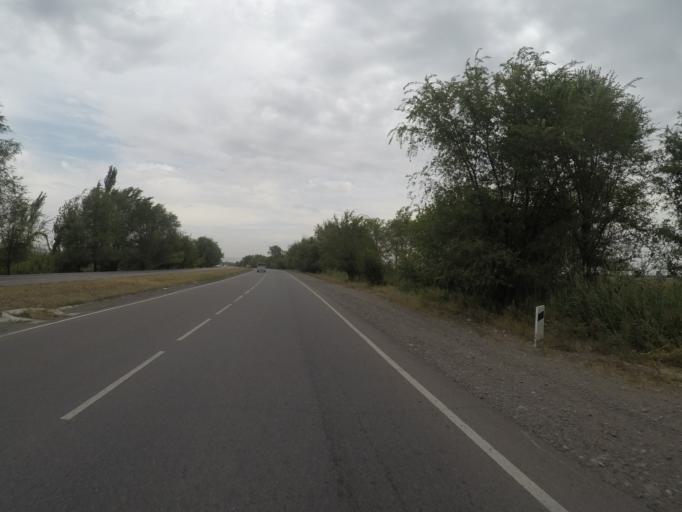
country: KG
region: Chuy
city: Kant
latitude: 42.9269
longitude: 74.7652
